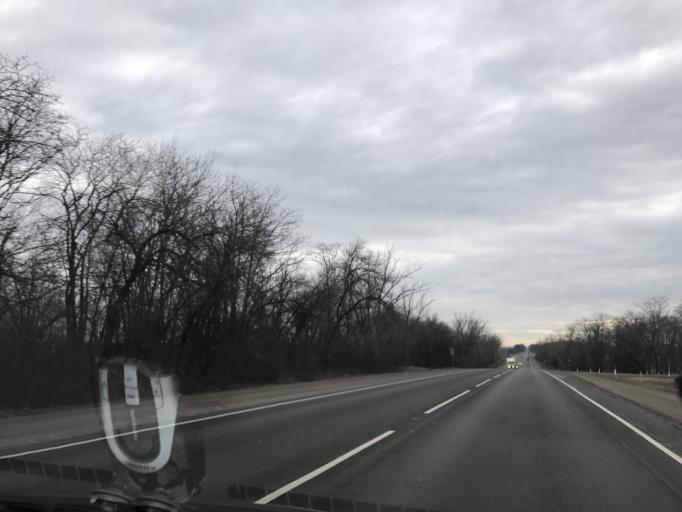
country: RU
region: Krasnodarskiy
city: Mirskoy
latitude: 45.6738
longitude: 40.3222
